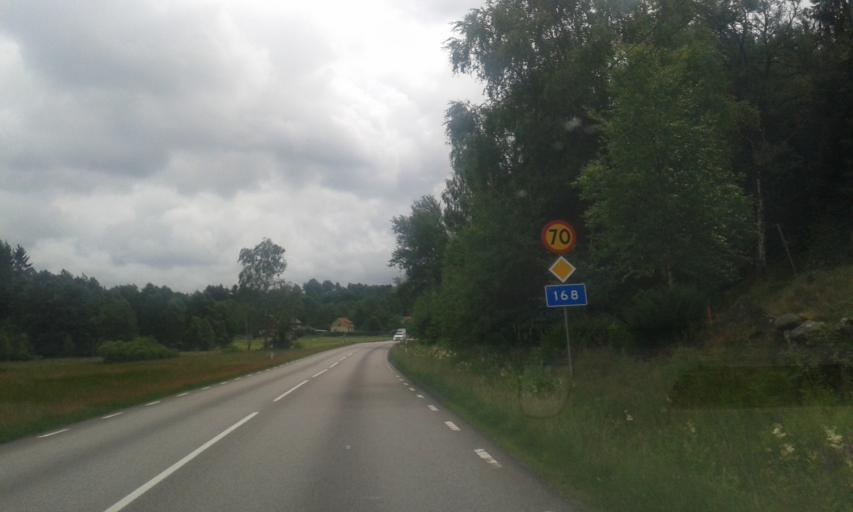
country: SE
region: Vaestra Goetaland
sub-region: Kungalvs Kommun
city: Kode
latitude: 57.8913
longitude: 11.8808
